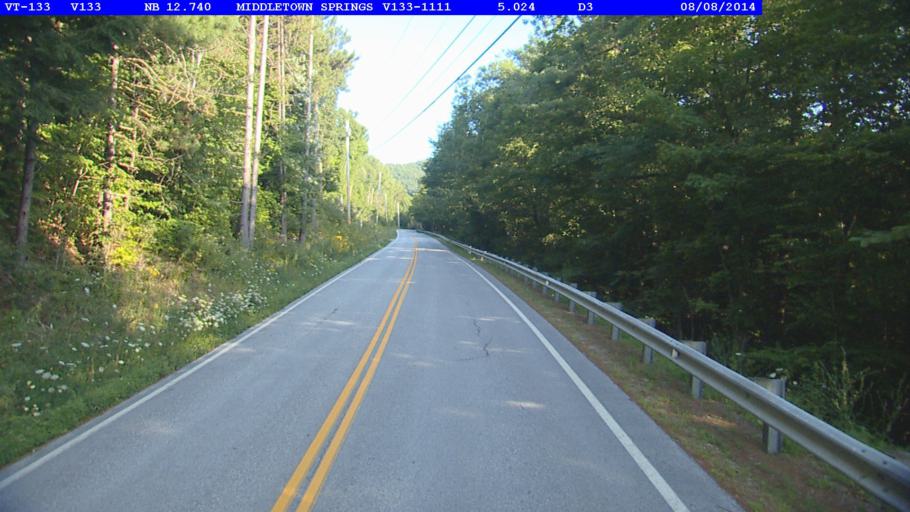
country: US
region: Vermont
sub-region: Rutland County
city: West Rutland
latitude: 43.4842
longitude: -73.0928
